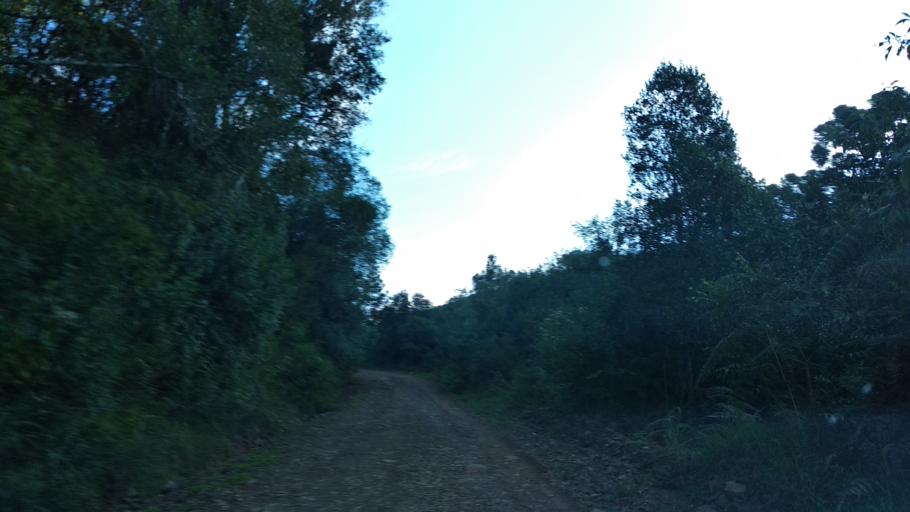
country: BR
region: Santa Catarina
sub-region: Celso Ramos
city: Celso Ramos
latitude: -27.5605
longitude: -51.2363
